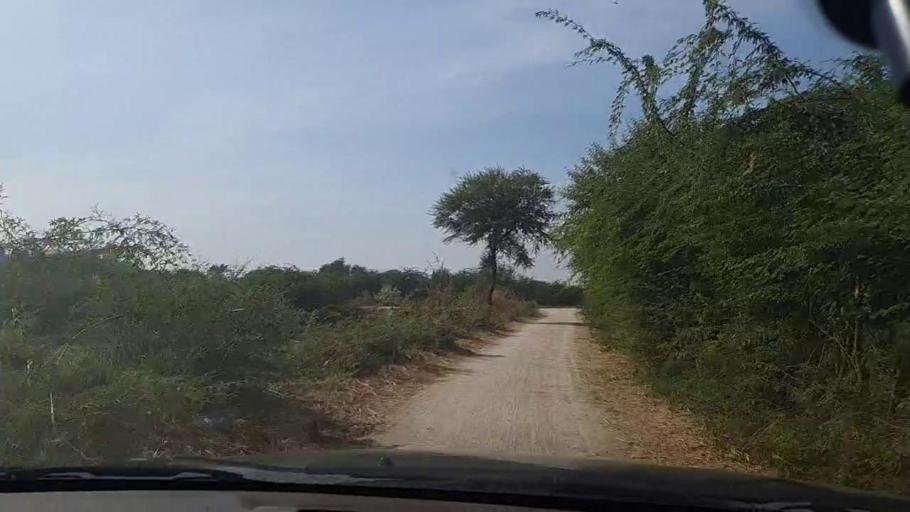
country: PK
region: Sindh
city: Mirpur Batoro
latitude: 24.7364
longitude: 68.2687
